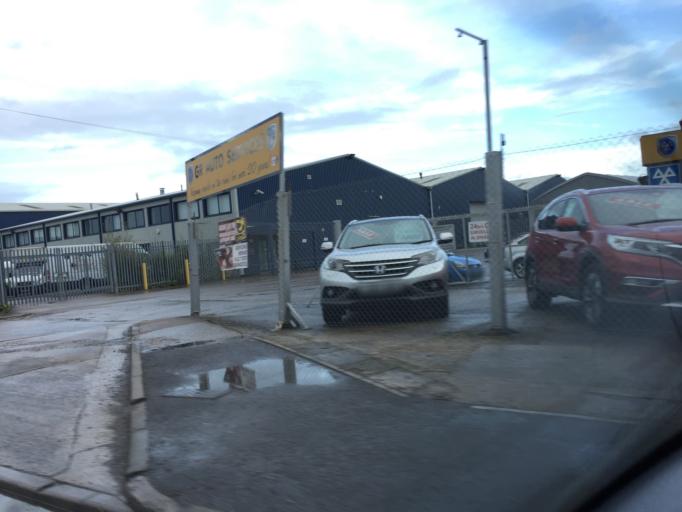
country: GB
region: England
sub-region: South Gloucestershire
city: Yate
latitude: 51.5430
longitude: -2.4335
